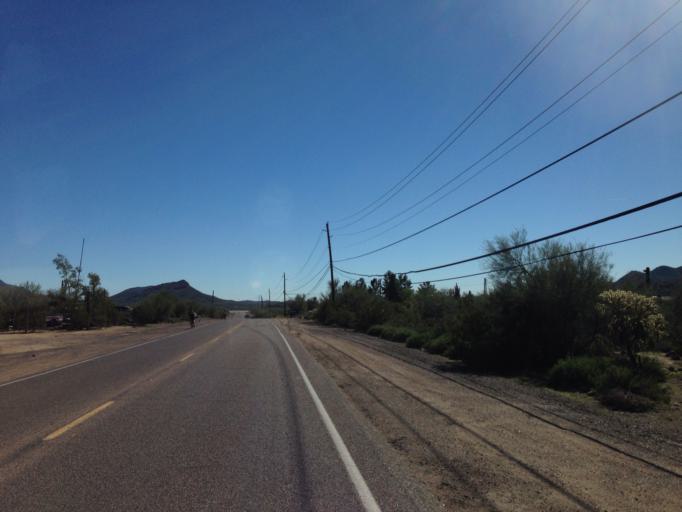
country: US
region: Arizona
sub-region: Maricopa County
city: New River
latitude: 33.9128
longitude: -112.0872
